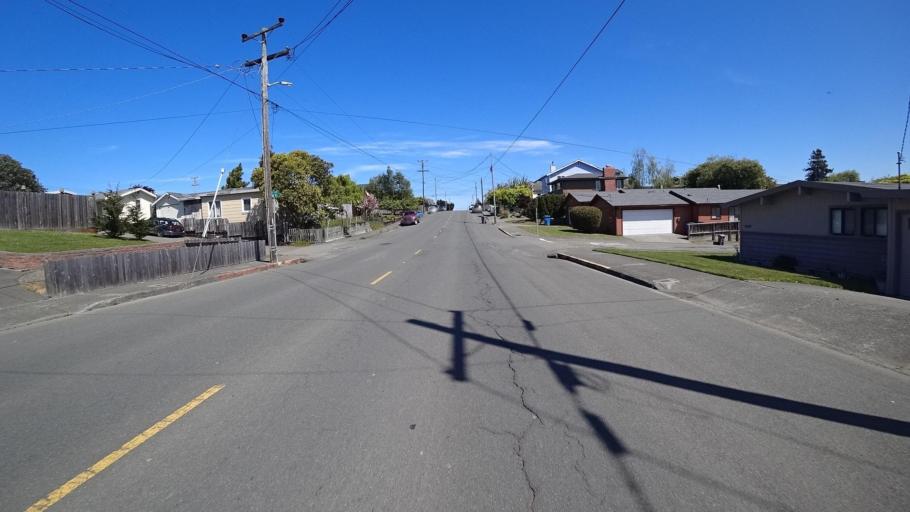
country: US
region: California
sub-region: Humboldt County
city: Myrtletown
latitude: 40.7925
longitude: -124.1482
